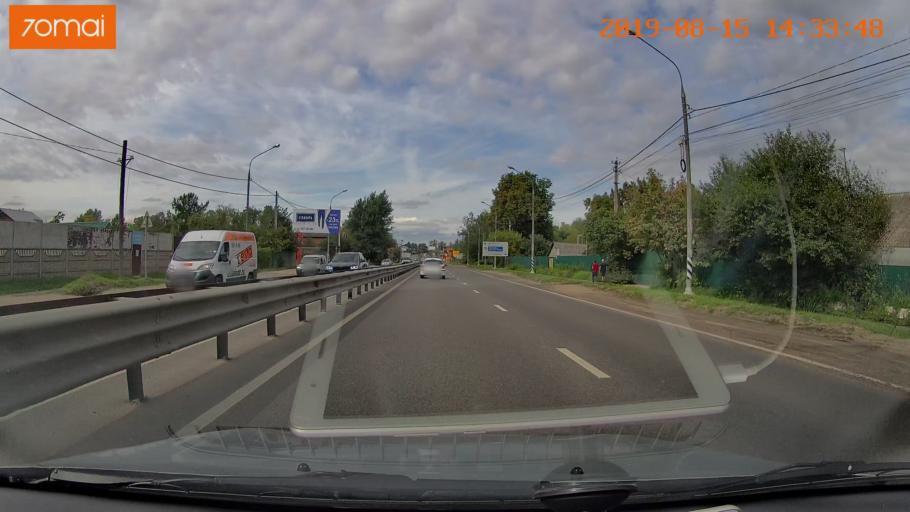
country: RU
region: Moskovskaya
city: Tomilino
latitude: 55.6361
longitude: 37.9394
